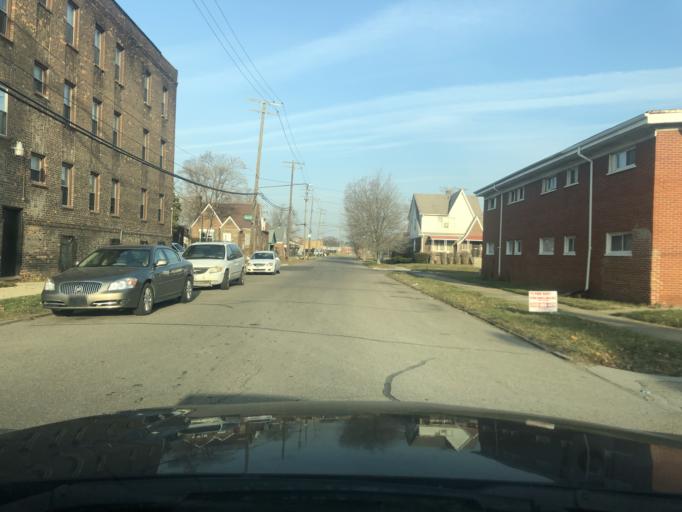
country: US
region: Michigan
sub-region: Wayne County
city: Highland Park
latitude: 42.3954
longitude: -83.1304
